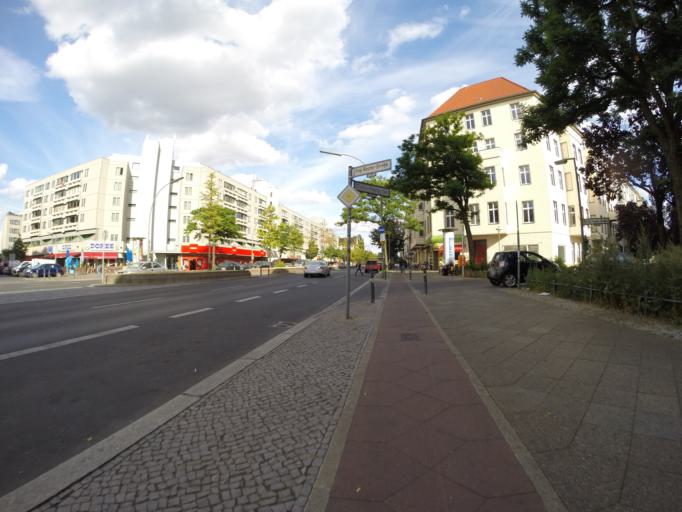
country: DE
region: Berlin
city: Berlin Schoeneberg
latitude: 52.4811
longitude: 13.3496
